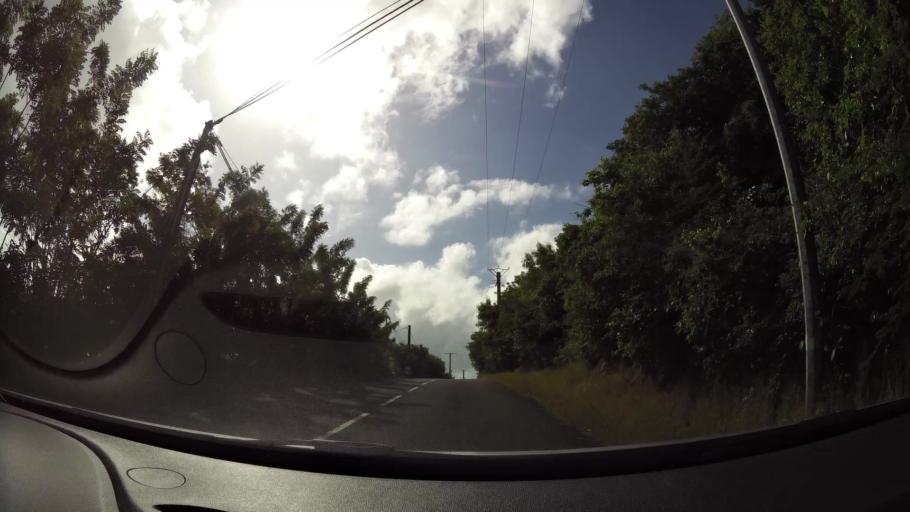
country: MQ
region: Martinique
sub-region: Martinique
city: Le Marin
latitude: 14.4261
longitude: -60.8749
